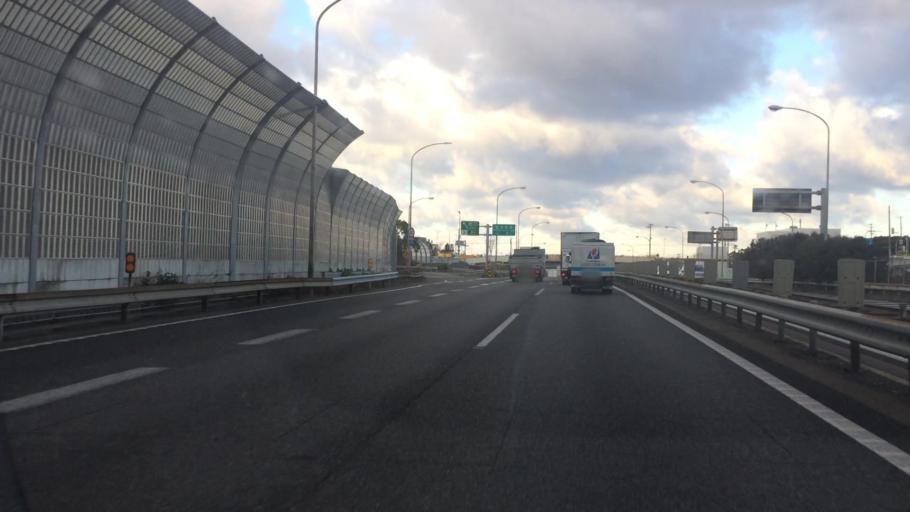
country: JP
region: Hyogo
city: Akashi
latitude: 34.6472
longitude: 135.0549
